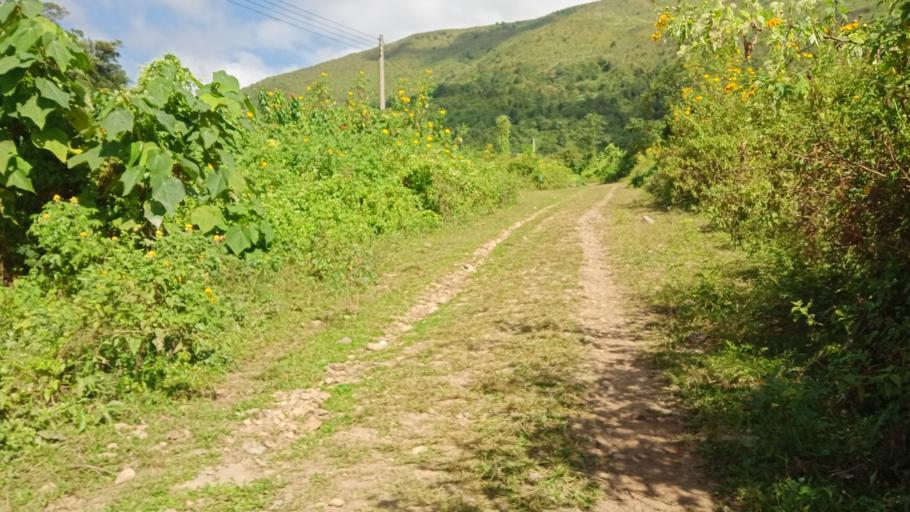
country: LA
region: Xiangkhoang
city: Phonsavan
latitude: 19.1140
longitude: 102.9249
